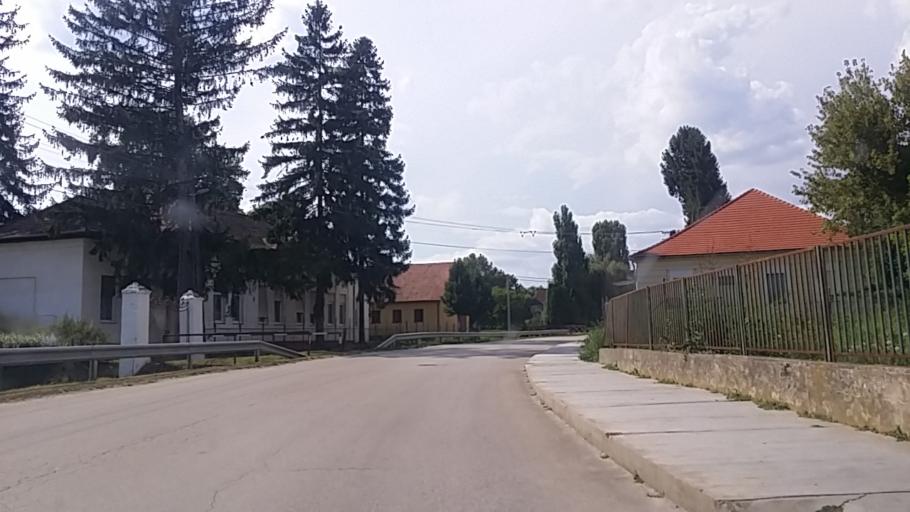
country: HU
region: Tolna
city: Gyonk
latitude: 46.5557
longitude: 18.4765
